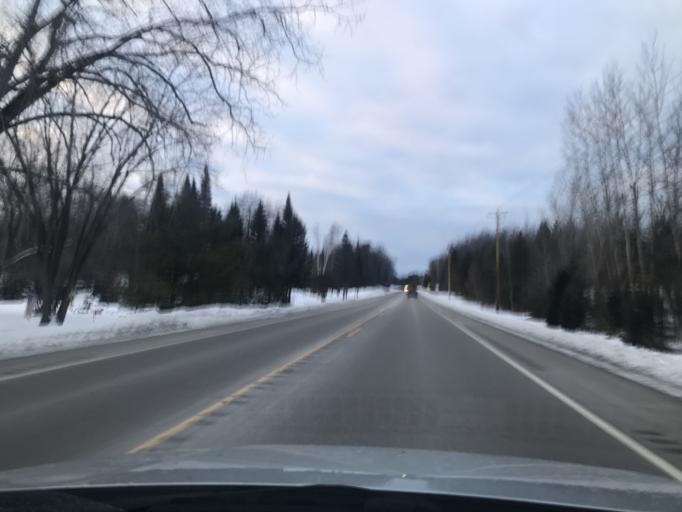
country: US
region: Wisconsin
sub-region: Marinette County
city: Peshtigo
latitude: 45.1630
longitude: -87.7252
